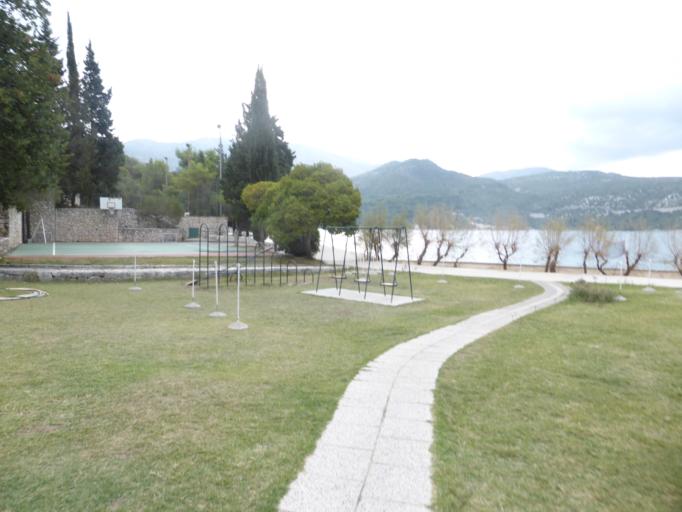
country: HR
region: Dubrovacko-Neretvanska
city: Podgora
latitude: 42.7797
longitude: 17.8702
